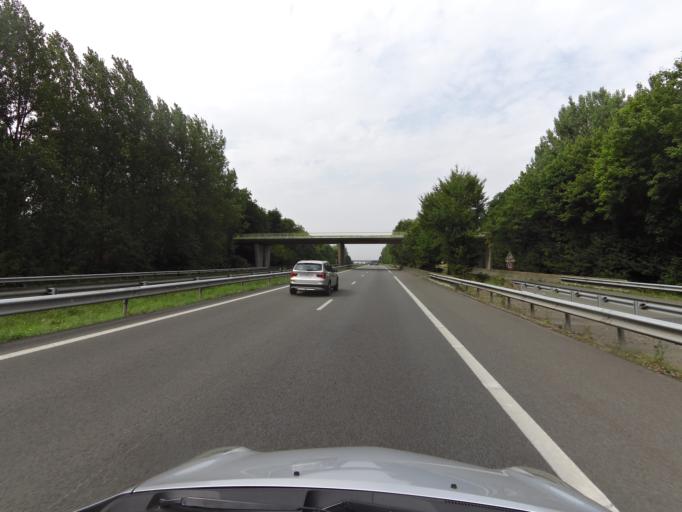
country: FR
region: Nord-Pas-de-Calais
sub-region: Departement du Nord
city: Marcoing
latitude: 50.0683
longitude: 3.1775
